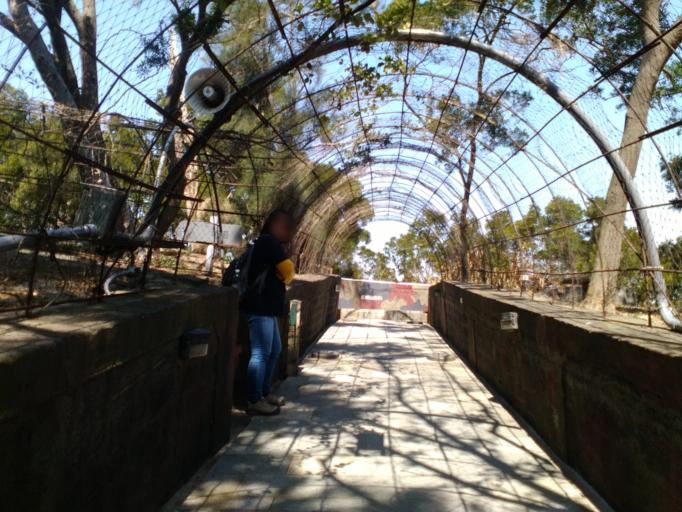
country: TW
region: Fukien
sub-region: Kinmen
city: Jincheng
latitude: 24.4472
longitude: 118.2551
